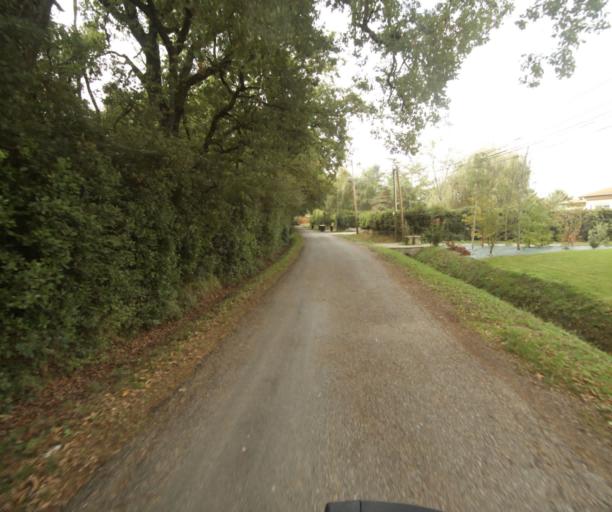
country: FR
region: Midi-Pyrenees
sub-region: Departement du Tarn-et-Garonne
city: Montech
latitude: 43.9567
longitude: 1.2505
